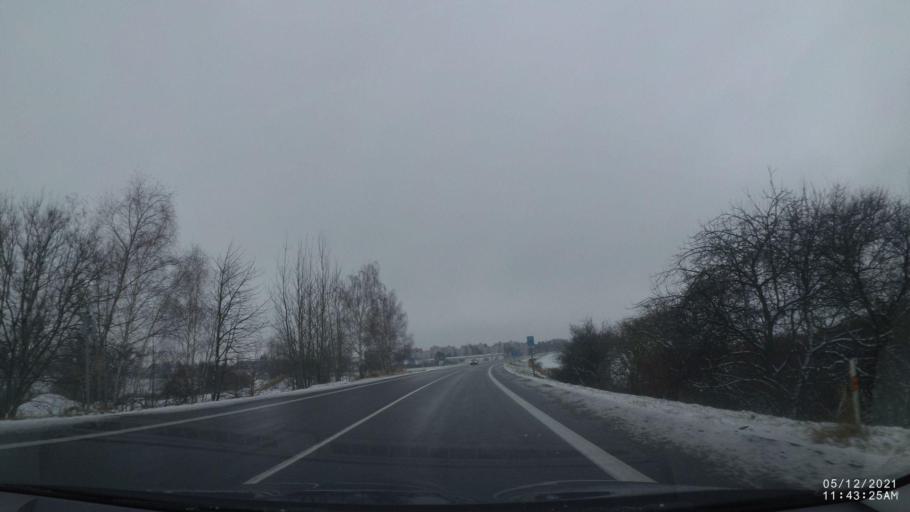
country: CZ
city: Dobruska
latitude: 50.2861
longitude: 16.1718
